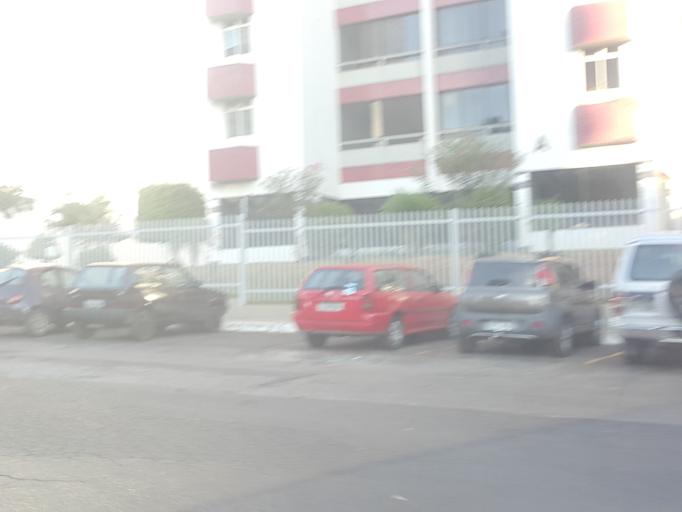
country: BR
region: Federal District
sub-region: Brasilia
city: Brasilia
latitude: -15.8349
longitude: -48.0201
